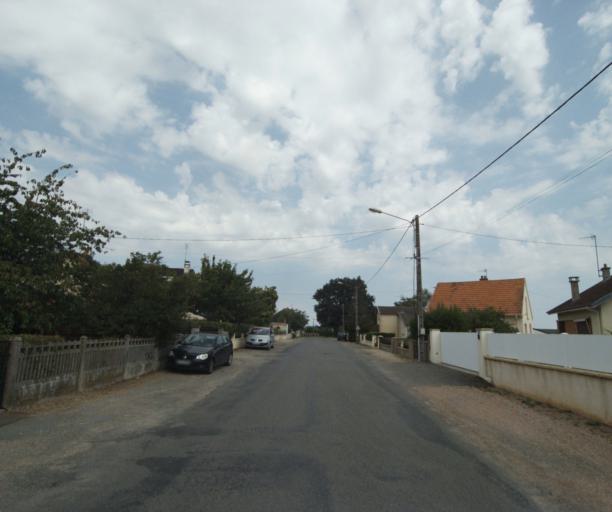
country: FR
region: Bourgogne
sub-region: Departement de Saone-et-Loire
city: Gueugnon
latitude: 46.5943
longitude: 4.0431
